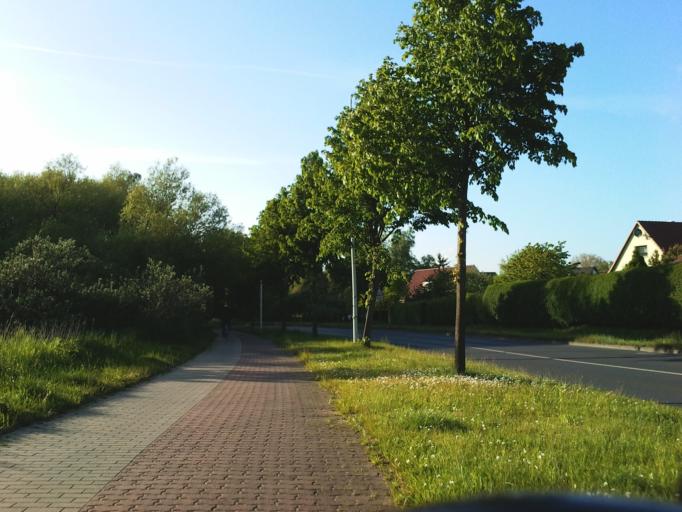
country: DE
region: Mecklenburg-Vorpommern
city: Dierkow-West
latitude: 54.1055
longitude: 12.1423
